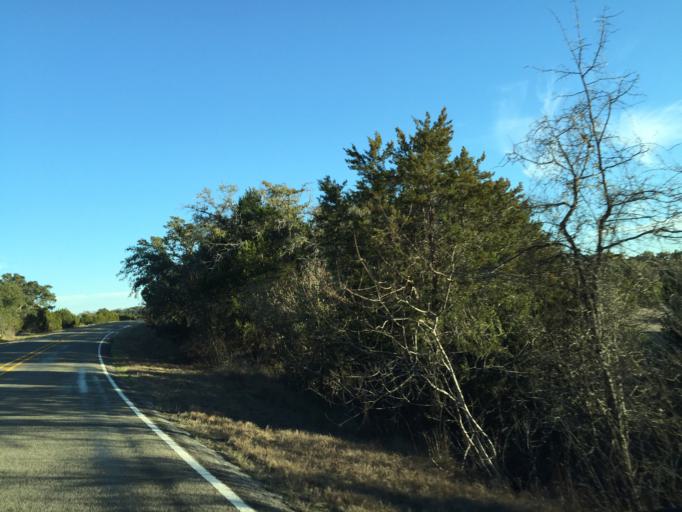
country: US
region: Texas
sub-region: Travis County
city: Lago Vista
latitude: 30.5210
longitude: -98.0470
